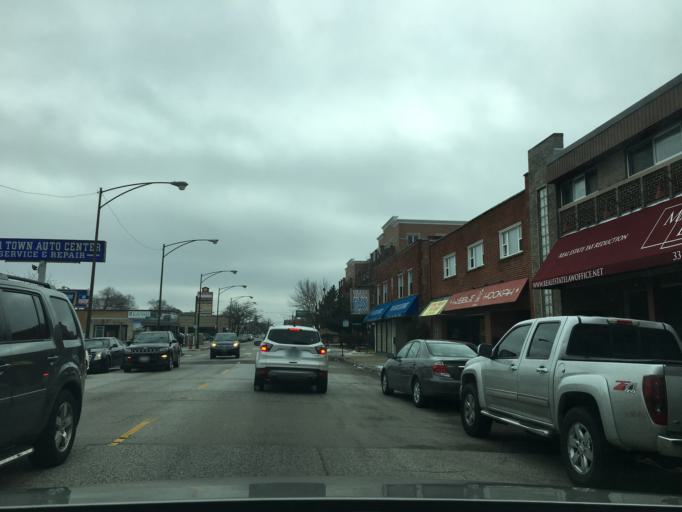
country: US
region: Illinois
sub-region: Cook County
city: Elmwood Park
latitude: 41.9404
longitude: -87.8068
